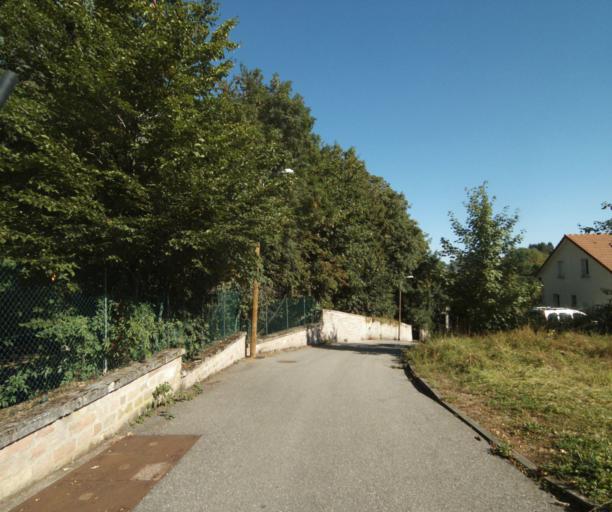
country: FR
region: Lorraine
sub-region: Departement des Vosges
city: Epinal
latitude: 48.1806
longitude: 6.4679
